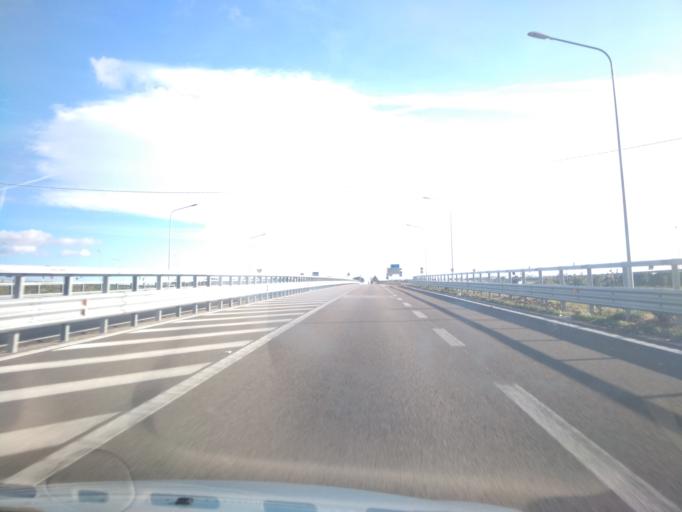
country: IT
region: Apulia
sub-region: Provincia di Bari
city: Gioia del Colle
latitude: 40.7568
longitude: 16.9583
